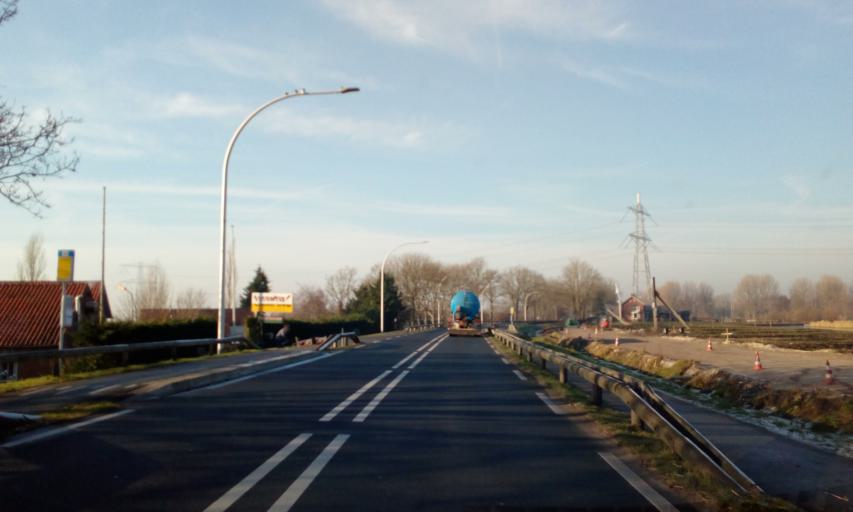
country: NL
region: South Holland
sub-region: Gemeente Vlist
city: Haastrecht
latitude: 52.0009
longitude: 4.7563
